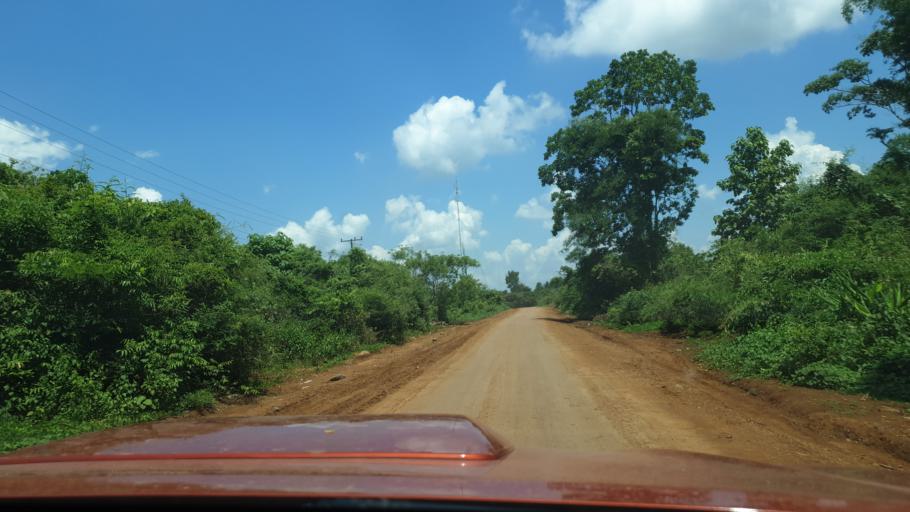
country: LA
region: Champasak
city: Champasak
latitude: 14.7825
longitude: 106.1291
